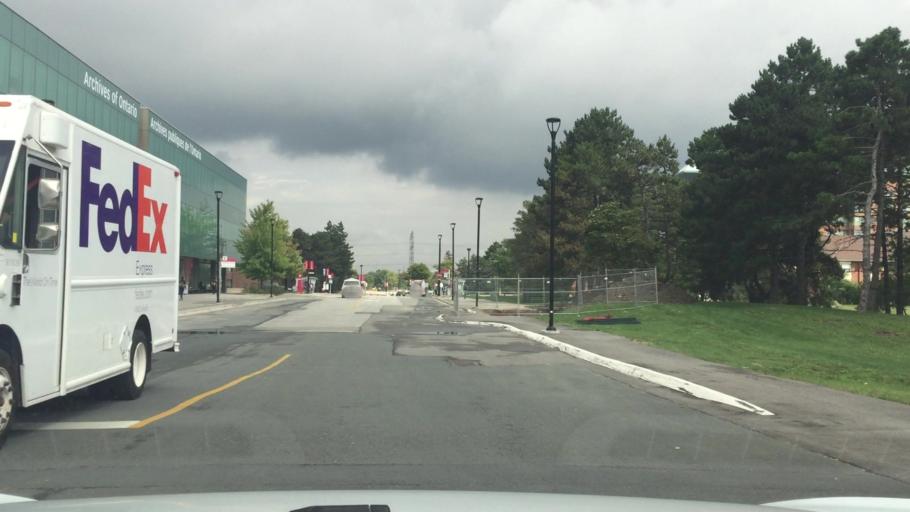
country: CA
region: Ontario
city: Concord
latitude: 43.7744
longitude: -79.4998
